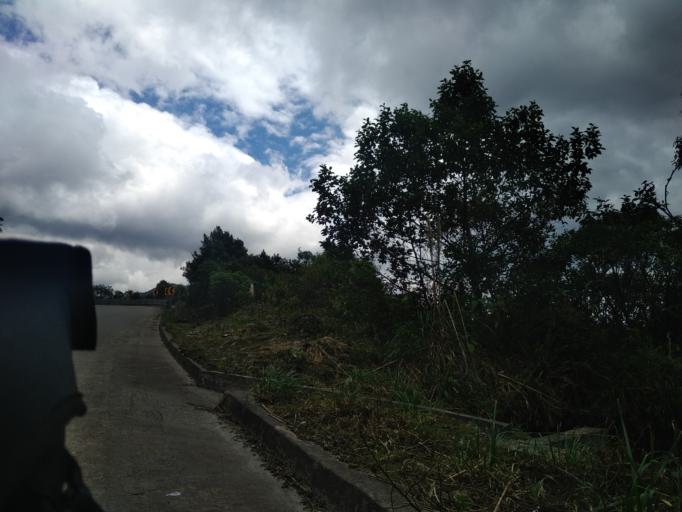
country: EC
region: Zamora-Chinchipe
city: Zamora
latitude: -4.4287
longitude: -79.1489
